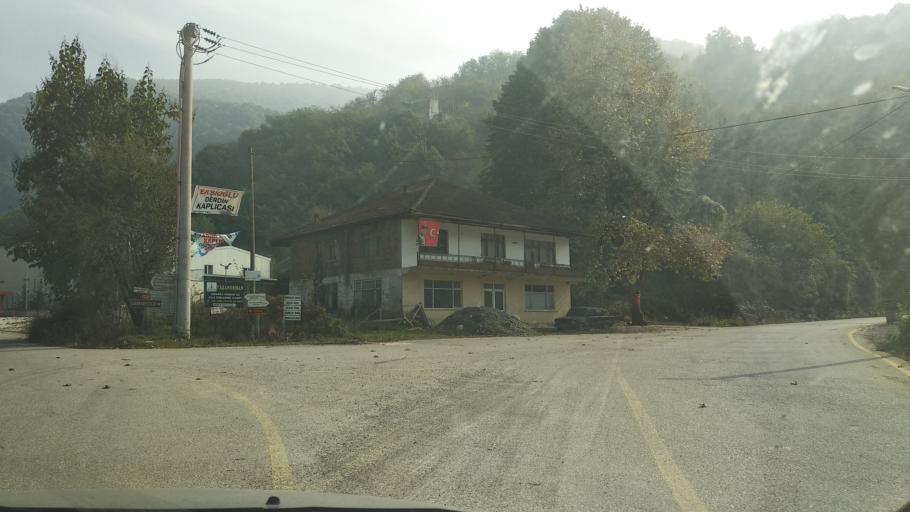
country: TR
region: Duzce
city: Duzce
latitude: 40.7368
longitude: 31.2078
